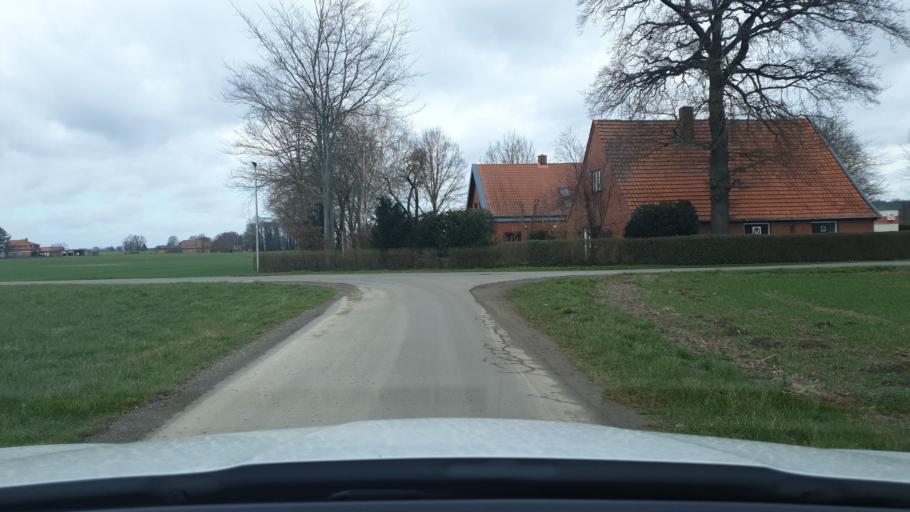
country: DE
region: North Rhine-Westphalia
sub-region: Regierungsbezirk Detmold
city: Hille
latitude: 52.3364
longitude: 8.7587
